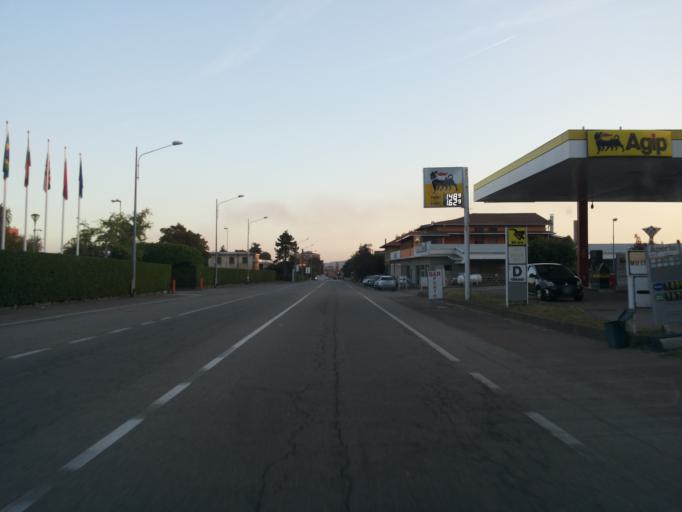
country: IT
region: Piedmont
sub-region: Provincia di Biella
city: Sandigliano
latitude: 45.5275
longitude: 8.0749
